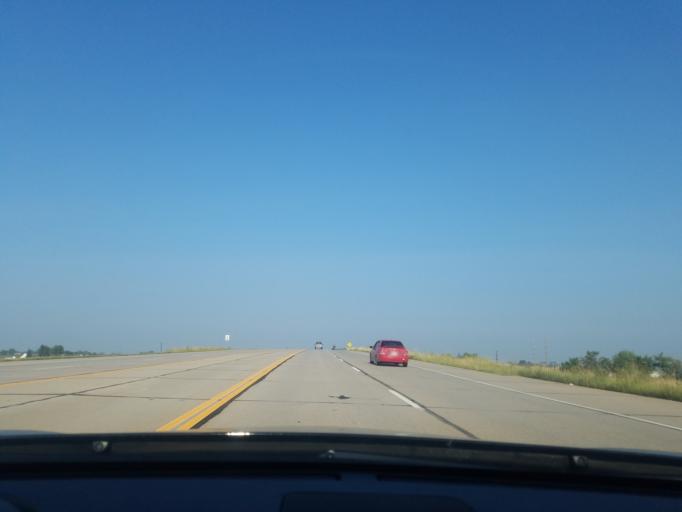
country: US
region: Colorado
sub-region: Larimer County
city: Campion
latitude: 40.3357
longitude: -105.0841
